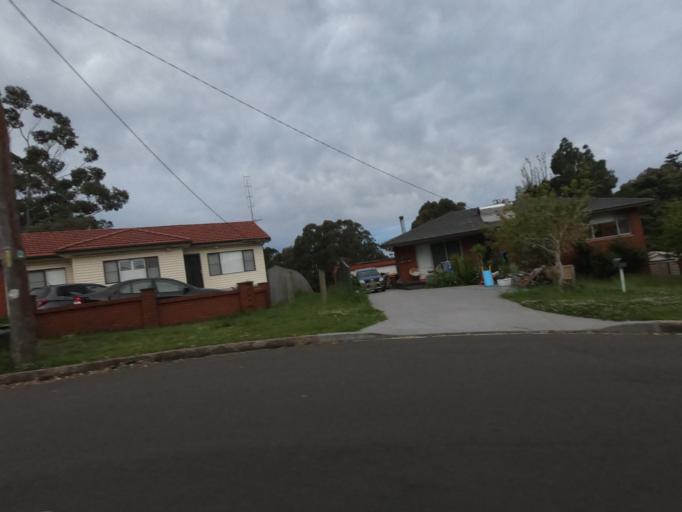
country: AU
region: New South Wales
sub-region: Wollongong
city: Lake Heights
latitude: -34.4836
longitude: 150.8658
